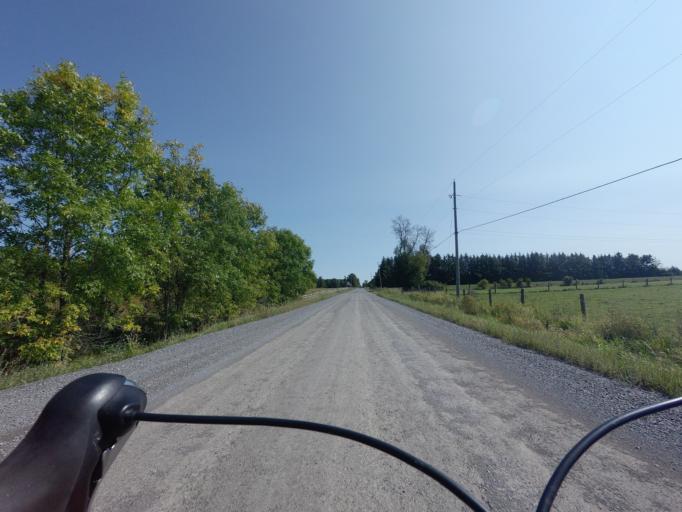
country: CA
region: Ontario
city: Arnprior
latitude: 45.3921
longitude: -76.1656
